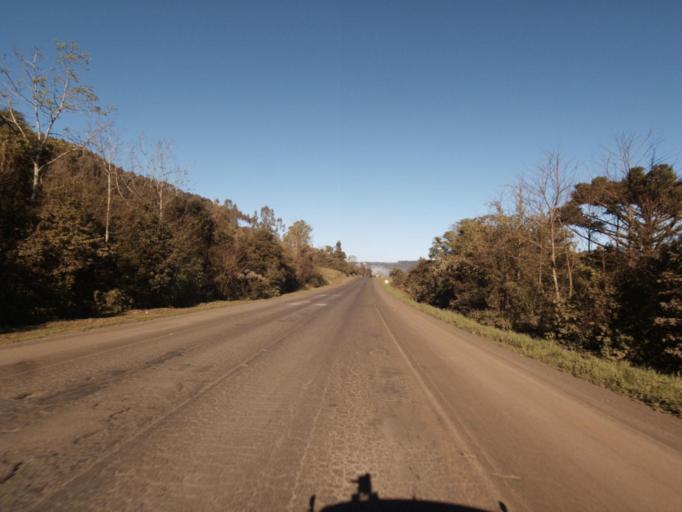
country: BR
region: Rio Grande do Sul
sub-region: Frederico Westphalen
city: Frederico Westphalen
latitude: -26.9606
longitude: -53.2063
